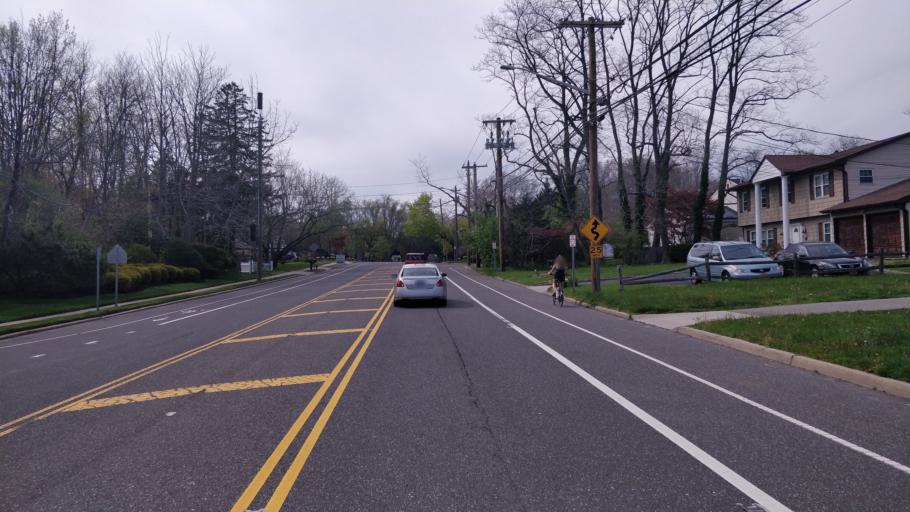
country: US
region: New York
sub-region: Suffolk County
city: Terryville
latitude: 40.9186
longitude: -73.0756
